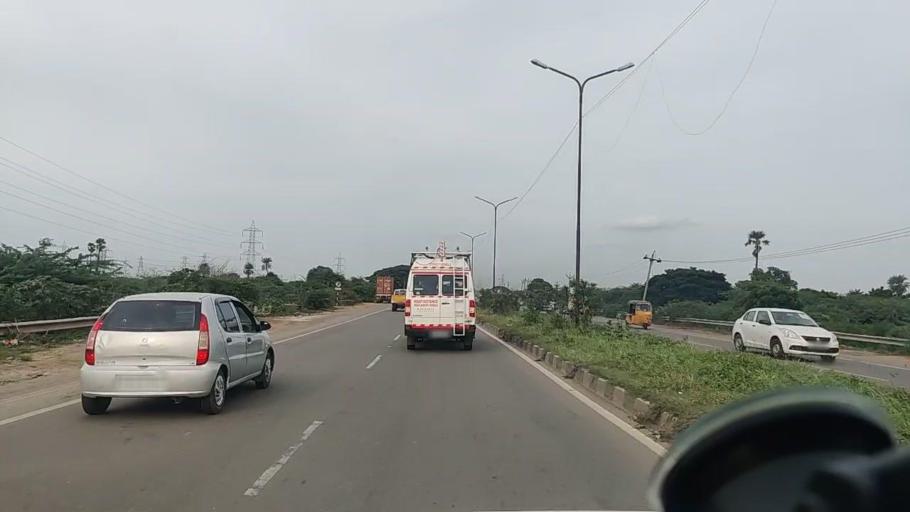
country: IN
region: Tamil Nadu
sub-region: Thiruvallur
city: Chinnasekkadu
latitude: 13.1734
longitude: 80.2366
